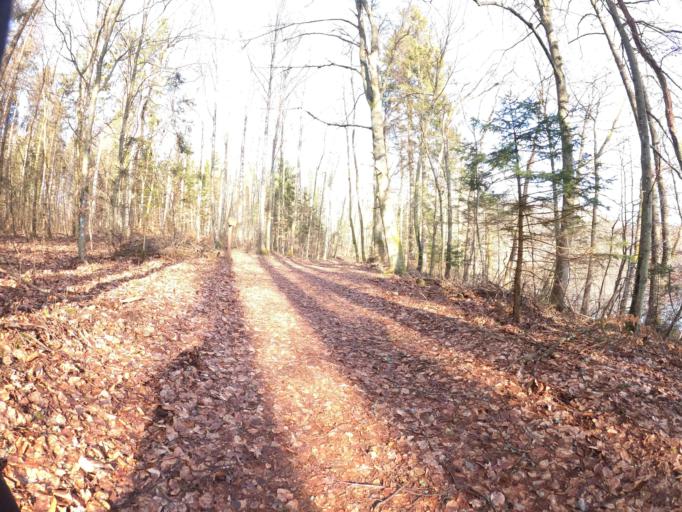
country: PL
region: West Pomeranian Voivodeship
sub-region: Powiat koszalinski
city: Polanow
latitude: 54.2172
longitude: 16.6945
